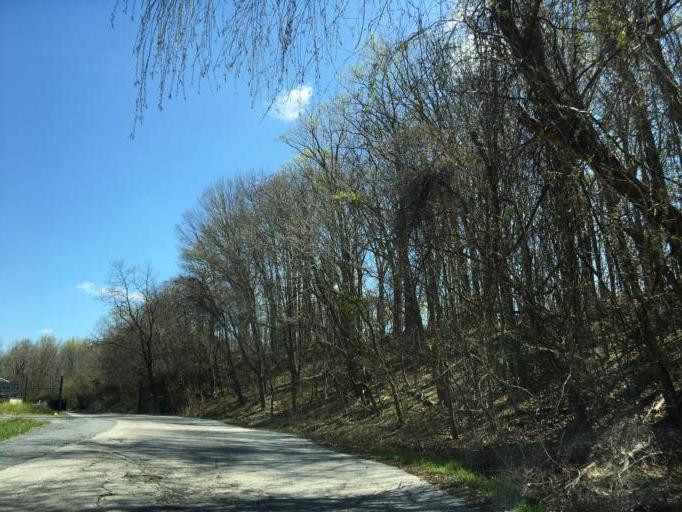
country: US
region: Maryland
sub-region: Baltimore County
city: Cockeysville
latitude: 39.4665
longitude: -76.6250
